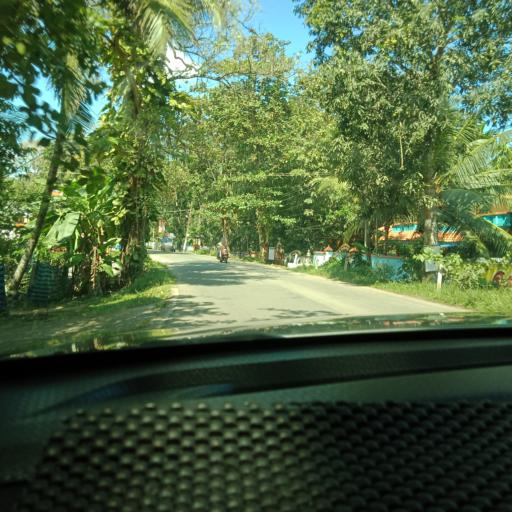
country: IN
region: Kerala
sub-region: Alappuzha
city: Mavelikara
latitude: 9.2993
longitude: 76.4559
